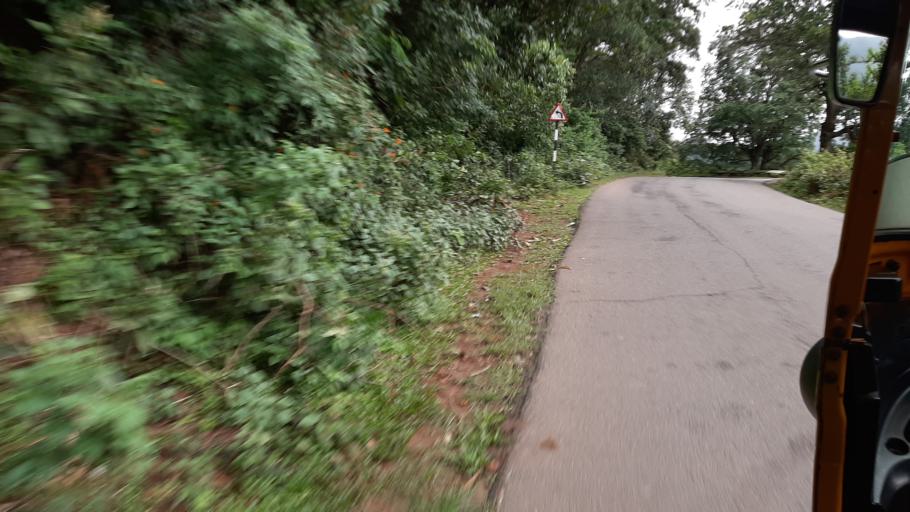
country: IN
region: Andhra Pradesh
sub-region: Vizianagaram District
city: Salur
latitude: 18.2457
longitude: 83.0210
